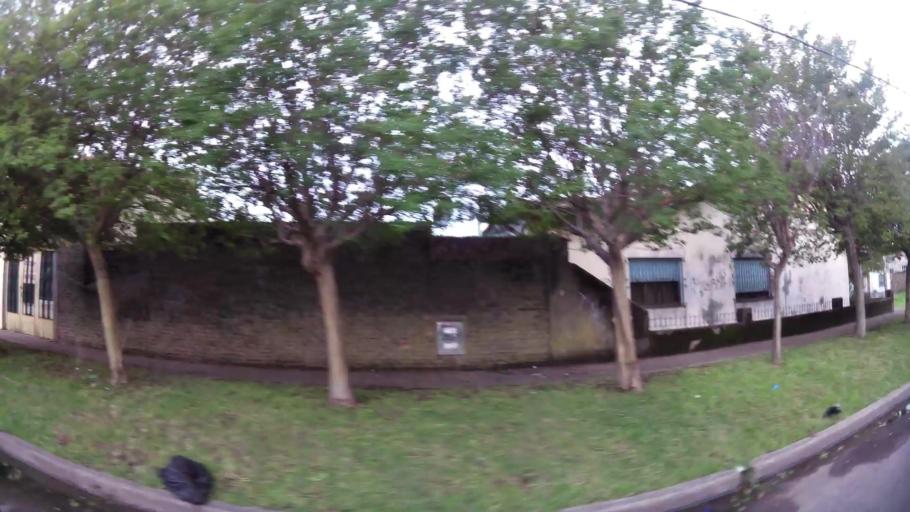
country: AR
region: Buenos Aires
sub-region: Partido de Lomas de Zamora
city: Lomas de Zamora
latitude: -34.7462
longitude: -58.3464
